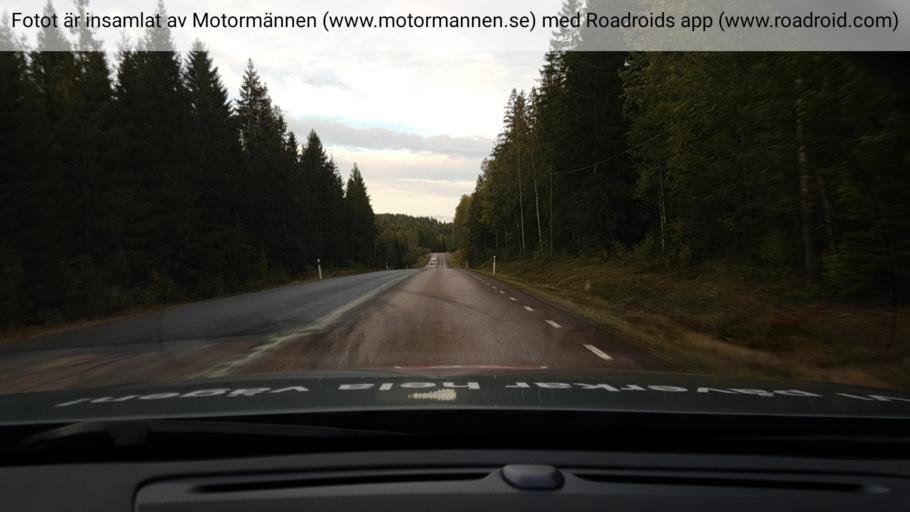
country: SE
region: Vaestra Goetaland
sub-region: Amals Kommun
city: Amal
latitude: 59.0558
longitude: 12.5018
